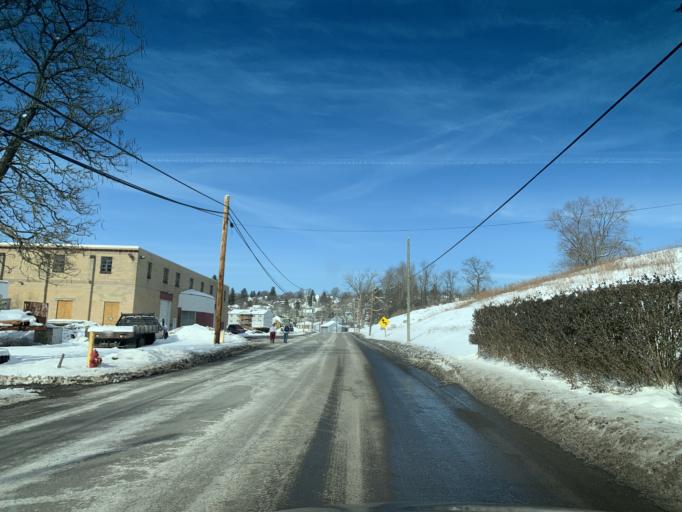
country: US
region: Maryland
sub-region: Allegany County
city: Frostburg
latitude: 39.6478
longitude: -78.9227
